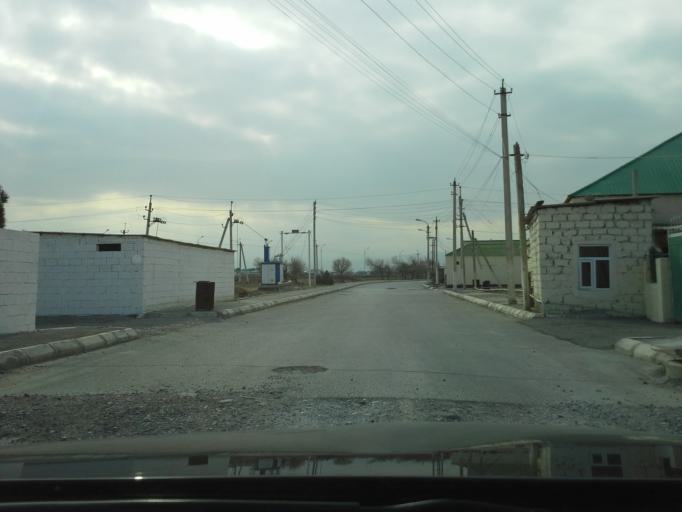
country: TM
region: Ahal
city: Abadan
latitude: 38.0399
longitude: 58.2774
